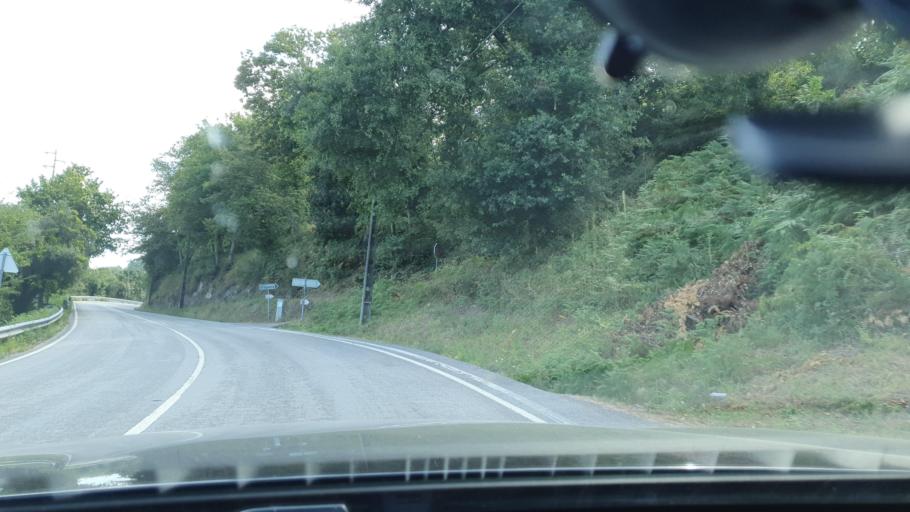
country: PT
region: Braga
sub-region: Vieira do Minho
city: Vieira do Minho
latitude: 41.6798
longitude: -8.1164
